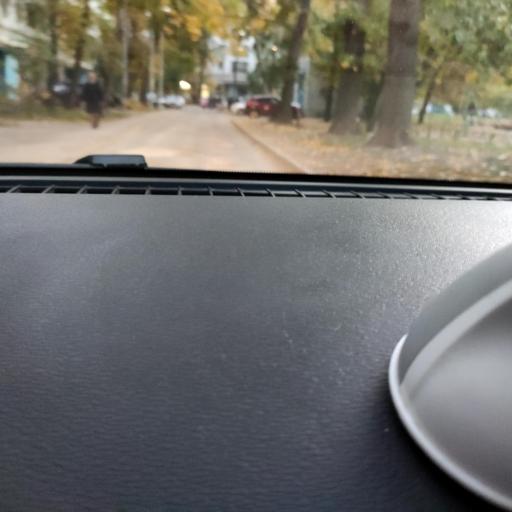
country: RU
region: Samara
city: Samara
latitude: 53.2325
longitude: 50.2126
